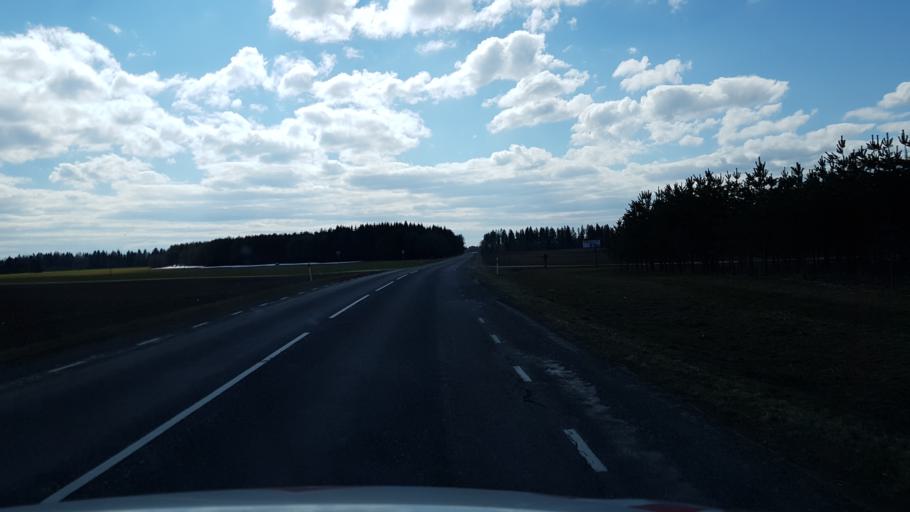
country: EE
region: Laeaene-Virumaa
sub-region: Rakvere linn
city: Rakvere
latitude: 59.2614
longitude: 26.2842
